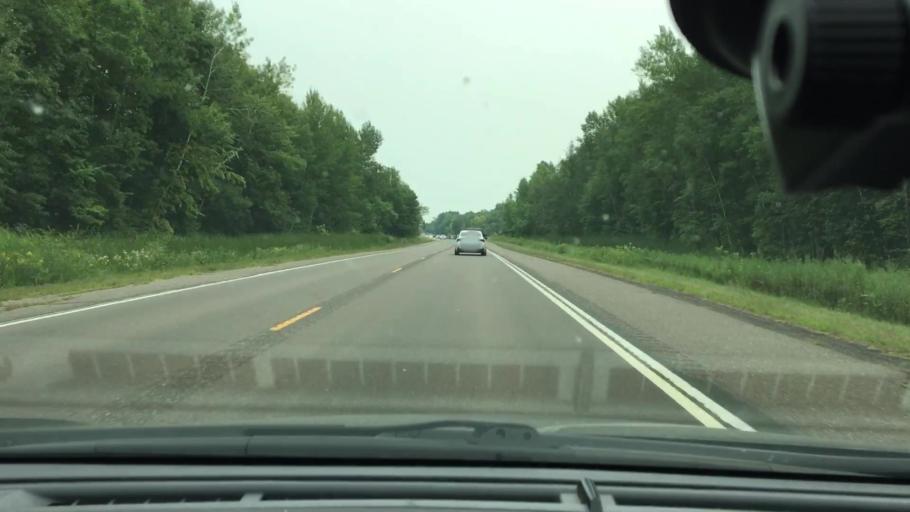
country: US
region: Minnesota
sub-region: Mille Lacs County
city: Vineland
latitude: 46.1505
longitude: -93.7414
